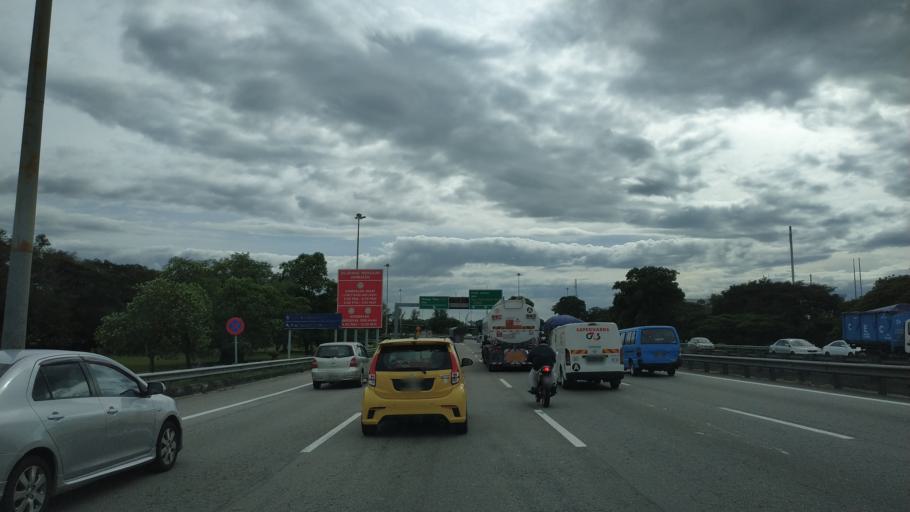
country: MY
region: Penang
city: Perai
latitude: 5.3707
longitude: 100.4002
